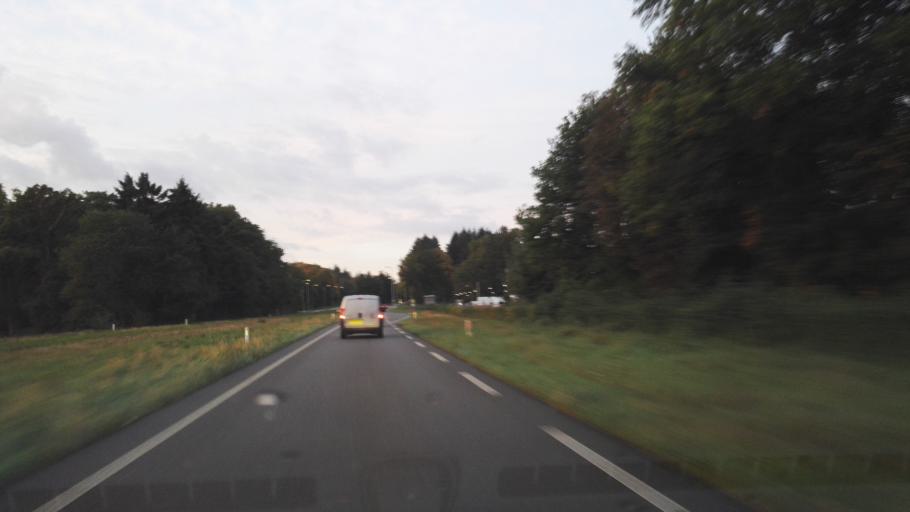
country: NL
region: Gelderland
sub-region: Gemeente Apeldoorn
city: Beekbergen
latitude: 52.1790
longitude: 5.9137
